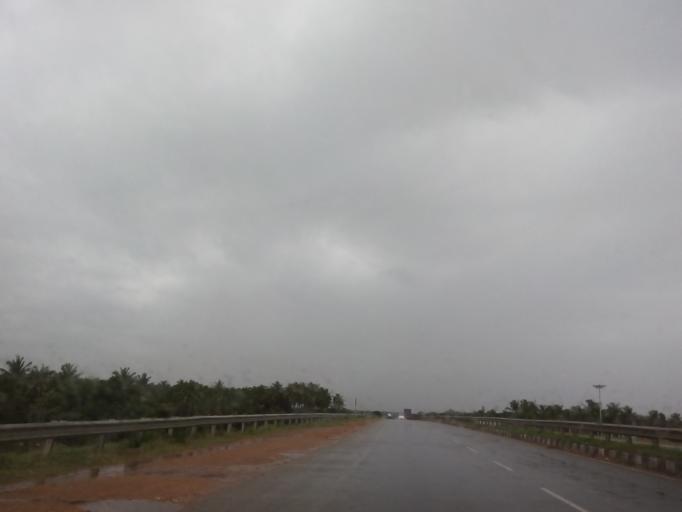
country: IN
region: Karnataka
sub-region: Davanagere
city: Harihar
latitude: 14.4355
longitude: 75.9594
